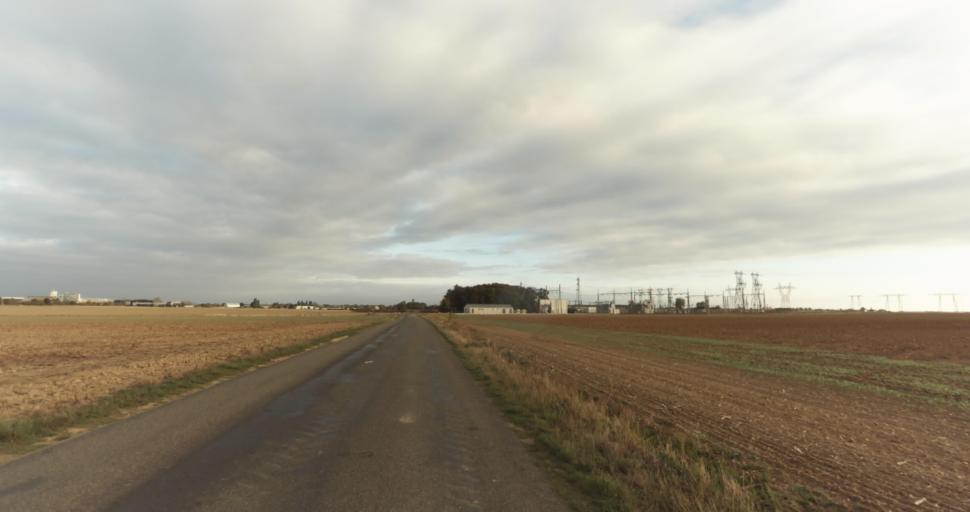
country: FR
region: Centre
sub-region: Departement d'Eure-et-Loir
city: Vernouillet
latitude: 48.7065
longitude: 1.3826
